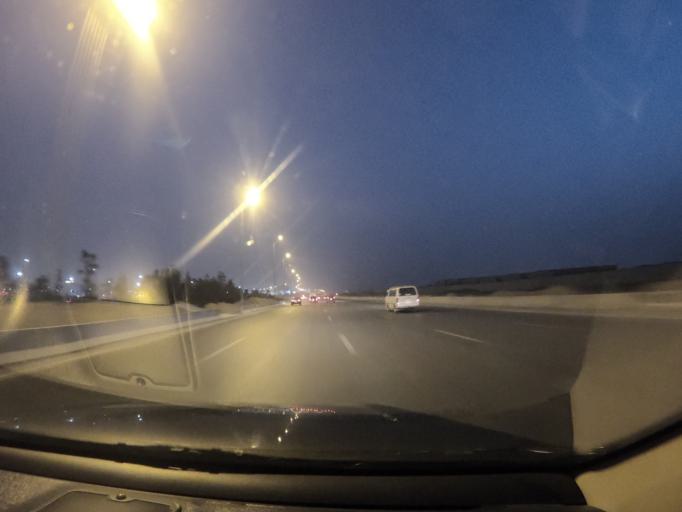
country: EG
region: Muhafazat al Qahirah
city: Cairo
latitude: 30.0347
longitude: 31.4024
